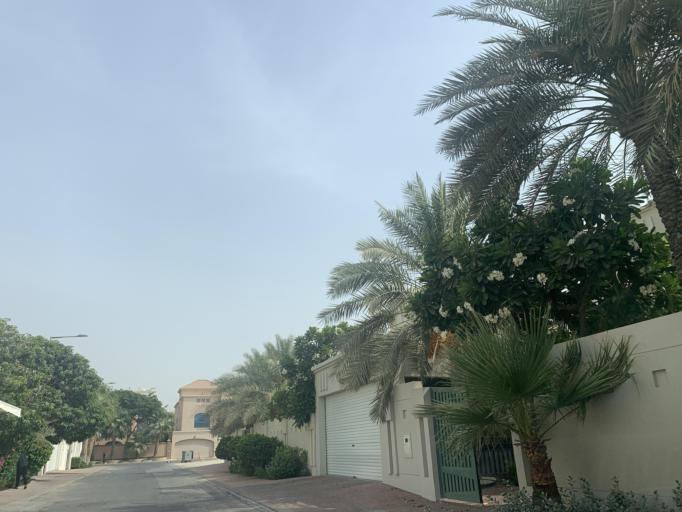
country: BH
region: Manama
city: Jidd Hafs
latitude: 26.2028
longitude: 50.4790
